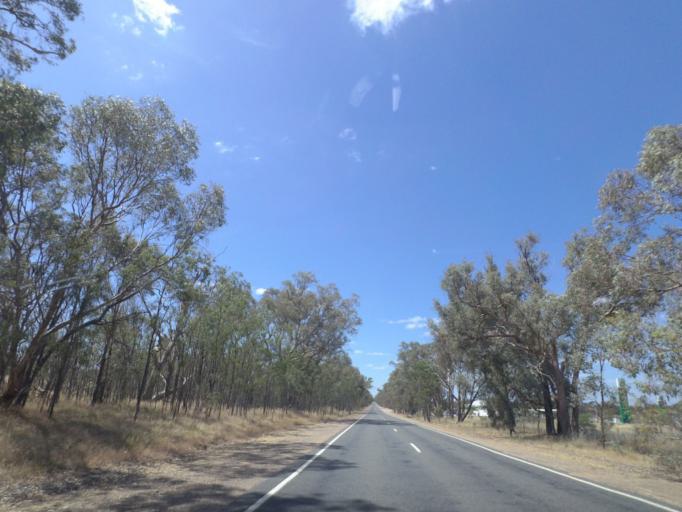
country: AU
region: Victoria
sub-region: Wangaratta
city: Wangaratta
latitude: -36.4403
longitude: 146.2462
